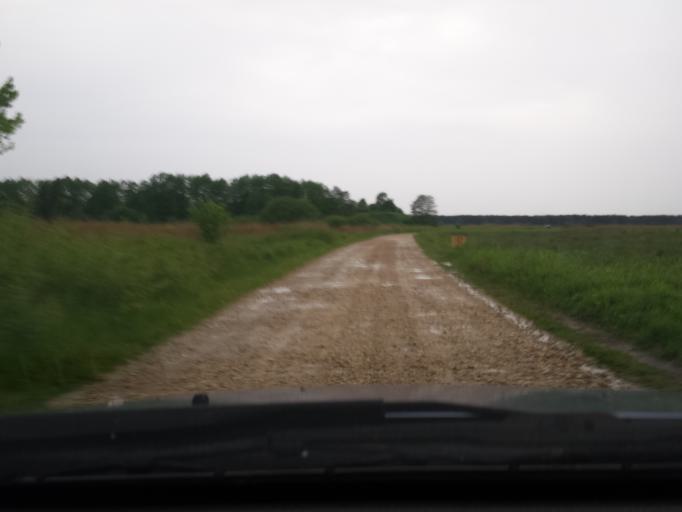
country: LV
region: Riga
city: Bolderaja
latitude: 57.0549
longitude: 24.0981
